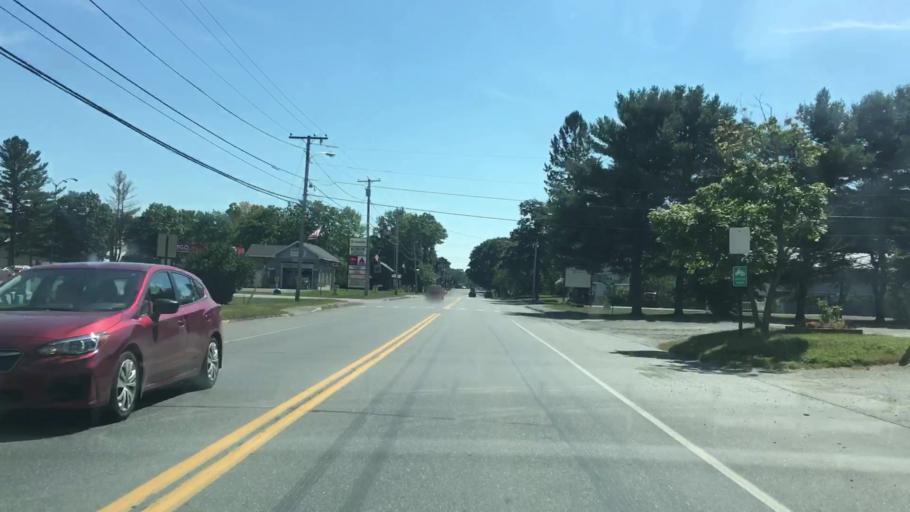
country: US
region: Maine
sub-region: Piscataquis County
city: Milo
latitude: 45.2591
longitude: -68.9877
